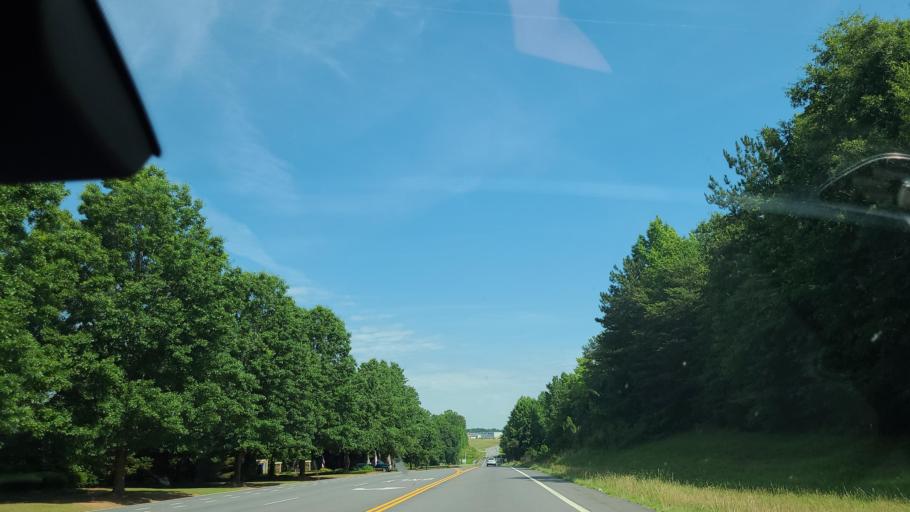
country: US
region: South Carolina
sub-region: Oconee County
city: Westminster
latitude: 34.6898
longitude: -83.0452
